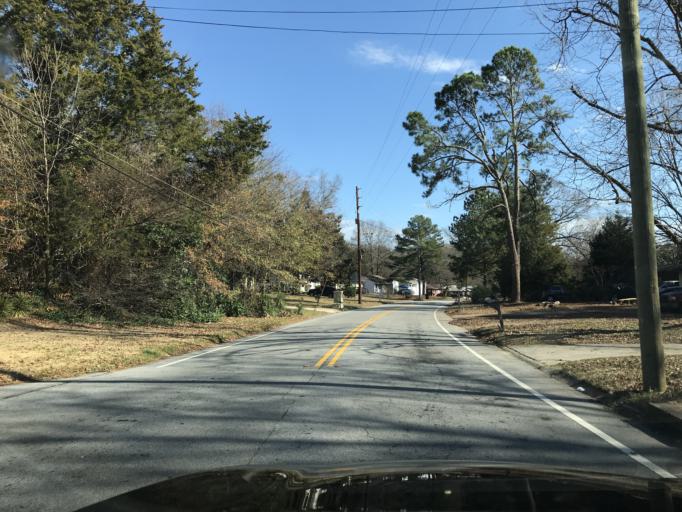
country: US
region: Georgia
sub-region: Clayton County
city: Morrow
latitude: 33.5801
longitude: -84.3732
